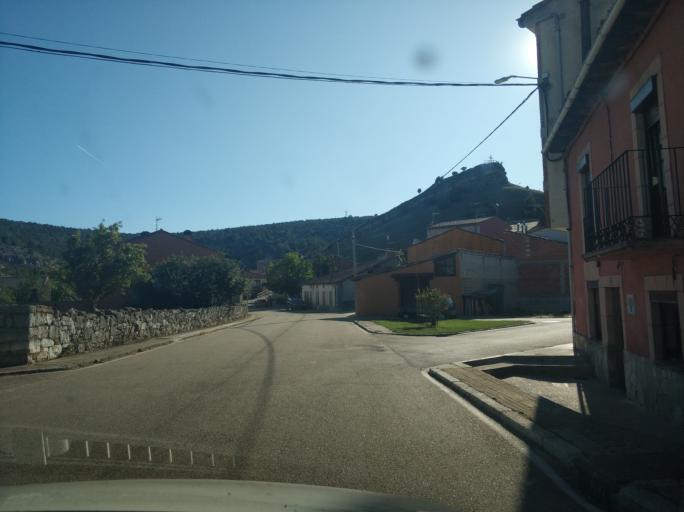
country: ES
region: Castille and Leon
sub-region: Provincia de Burgos
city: Hontoria del Pinar
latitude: 41.8455
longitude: -3.1651
